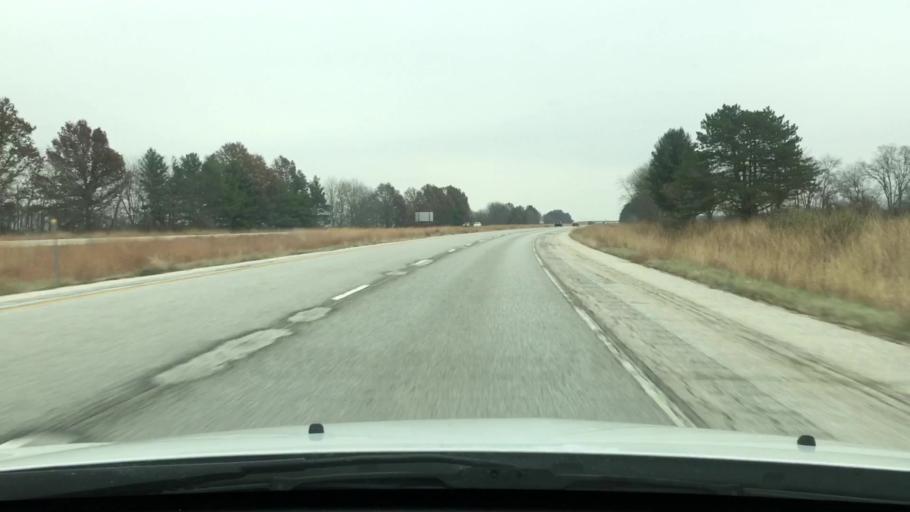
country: US
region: Illinois
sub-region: Morgan County
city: Jacksonville
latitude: 39.7373
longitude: -90.1475
